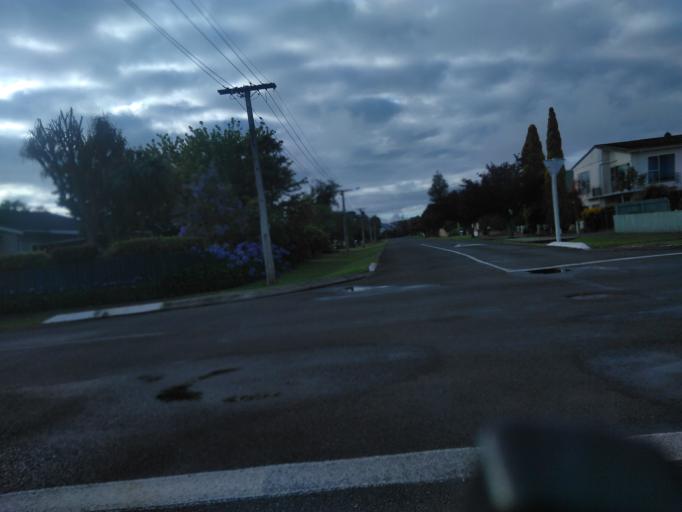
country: NZ
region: Gisborne
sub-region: Gisborne District
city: Gisborne
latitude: -38.6588
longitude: 178.0304
